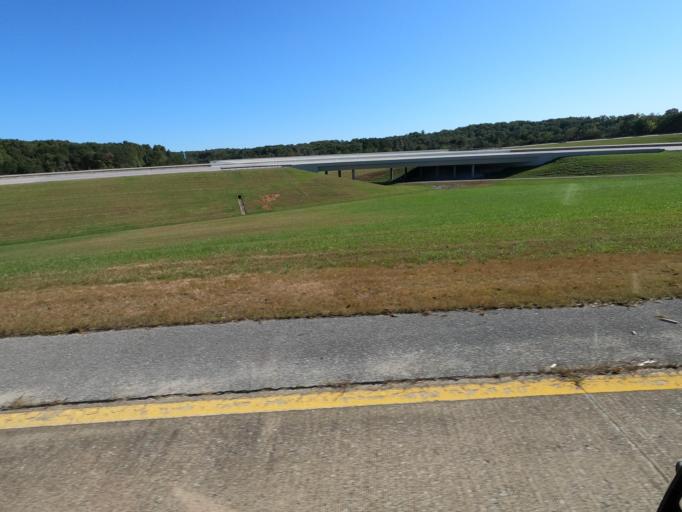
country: US
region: Tennessee
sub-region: Hamilton County
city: Soddy-Daisy
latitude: 35.3015
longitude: -85.1523
